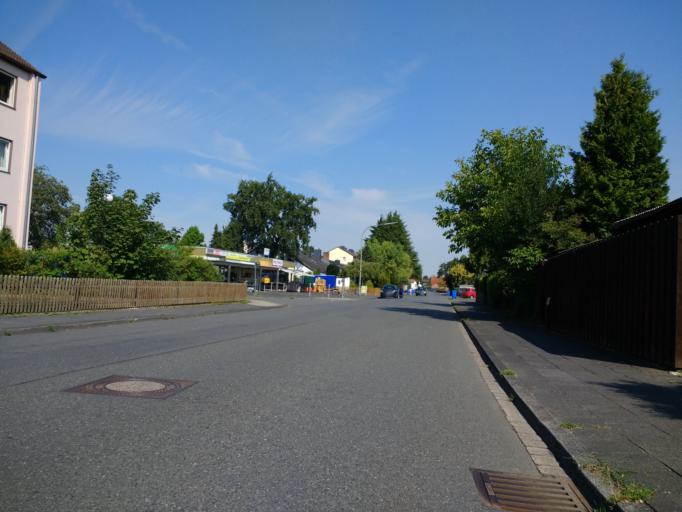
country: DE
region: Lower Saxony
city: Gifhorn
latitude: 52.4724
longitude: 10.5569
